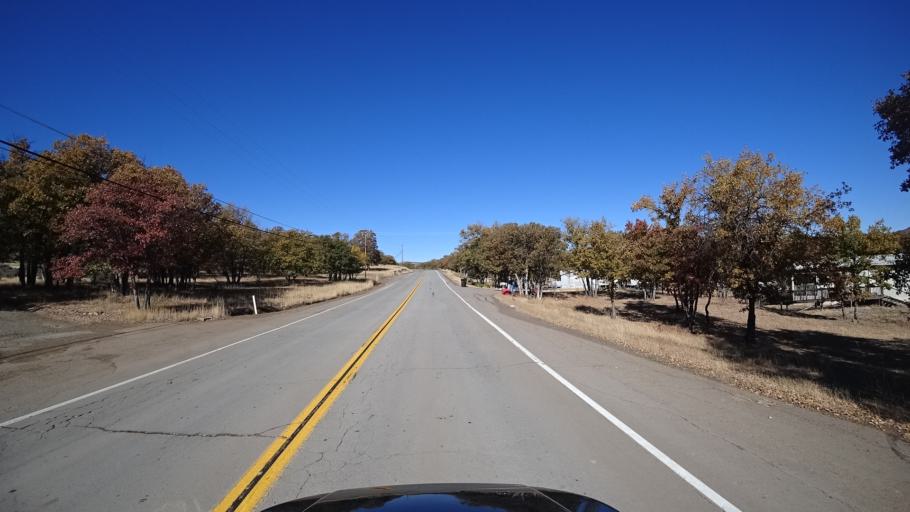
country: US
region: California
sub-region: Siskiyou County
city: Montague
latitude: 41.8878
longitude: -122.4924
